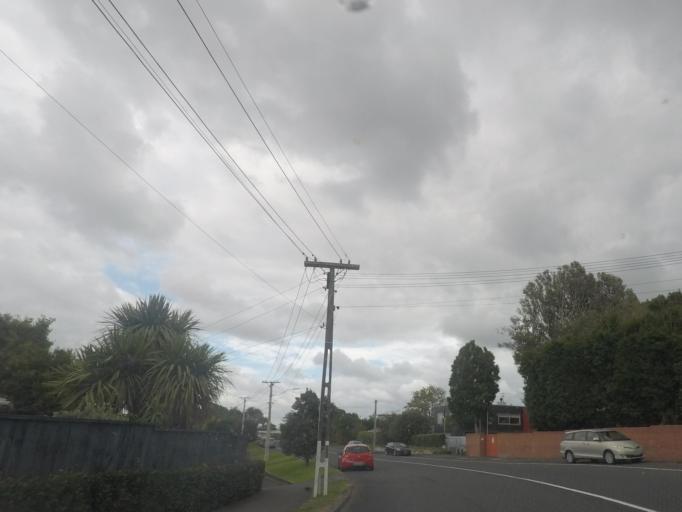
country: NZ
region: Auckland
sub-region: Auckland
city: Tamaki
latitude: -36.8686
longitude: 174.8774
